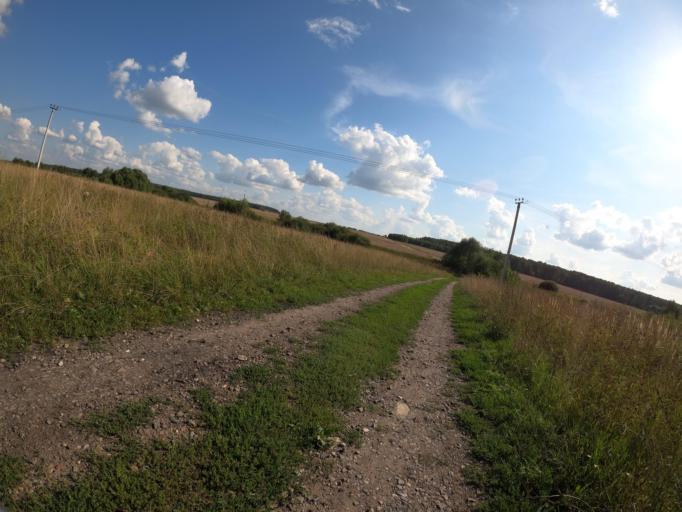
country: RU
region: Moskovskaya
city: Troitskoye
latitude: 55.2318
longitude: 38.4865
